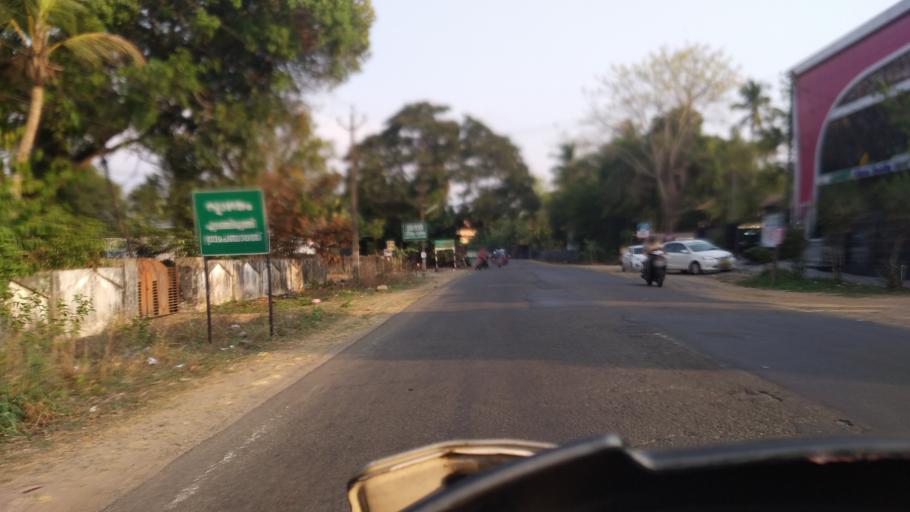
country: IN
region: Kerala
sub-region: Thrissur District
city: Thanniyam
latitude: 10.3637
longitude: 76.1245
